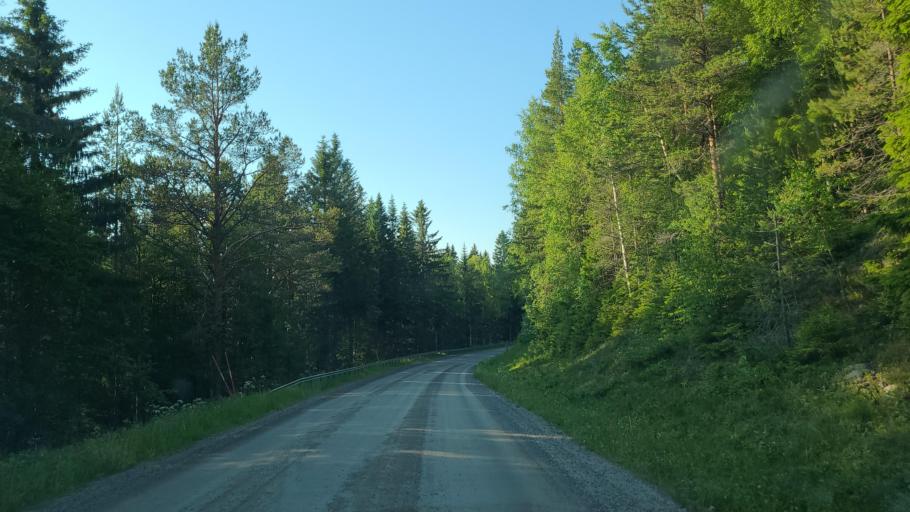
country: SE
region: Vaesterbotten
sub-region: Skelleftea Kommun
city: Burea
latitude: 64.3541
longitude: 21.3525
